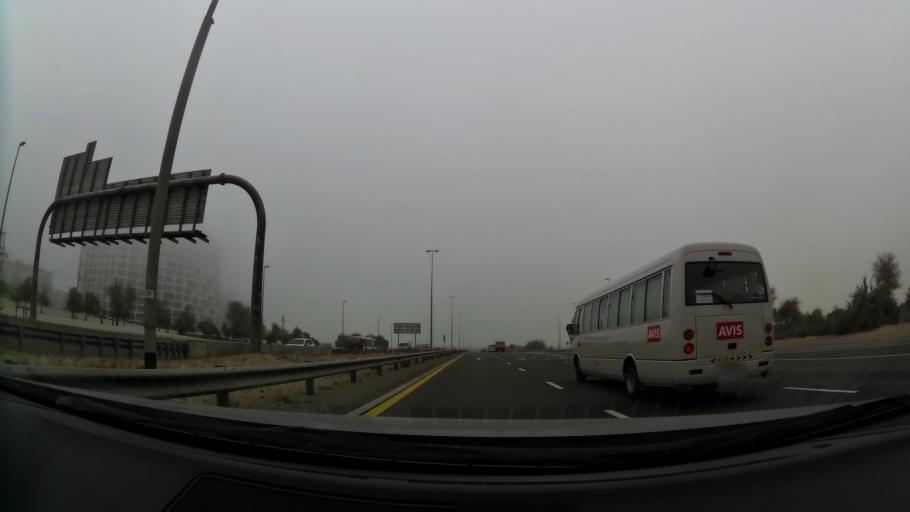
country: AE
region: Dubai
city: Dubai
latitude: 25.1087
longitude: 55.3744
